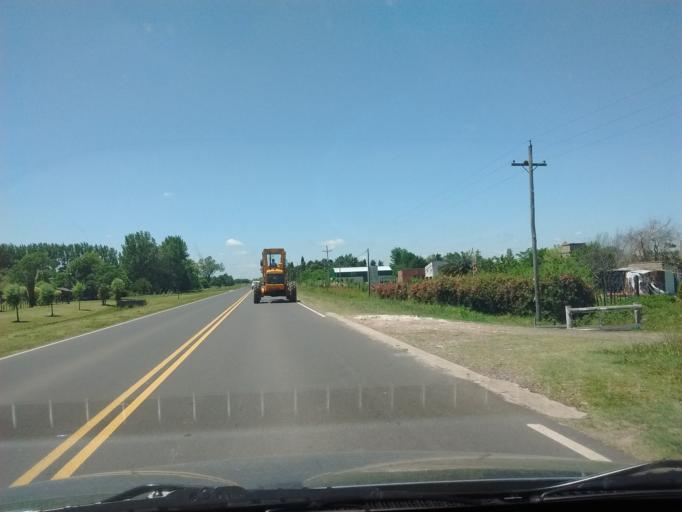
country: AR
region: Entre Rios
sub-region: Departamento de Gualeguay
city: Gualeguay
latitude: -33.1152
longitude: -59.3552
